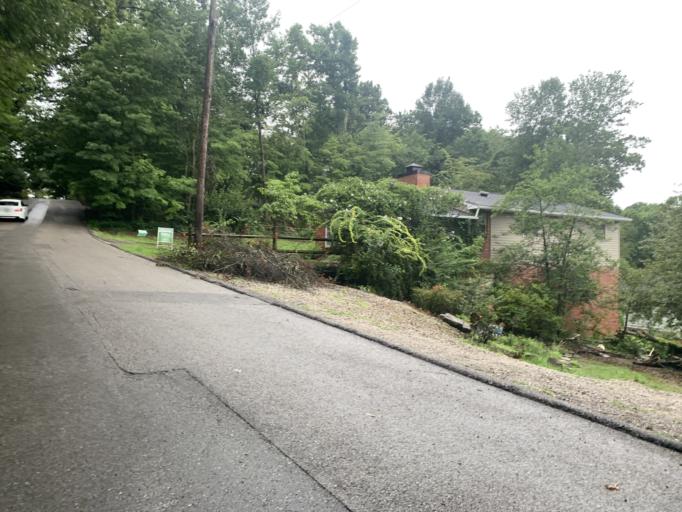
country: US
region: West Virginia
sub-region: Kanawha County
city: Charleston
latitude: 38.3425
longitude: -81.6406
